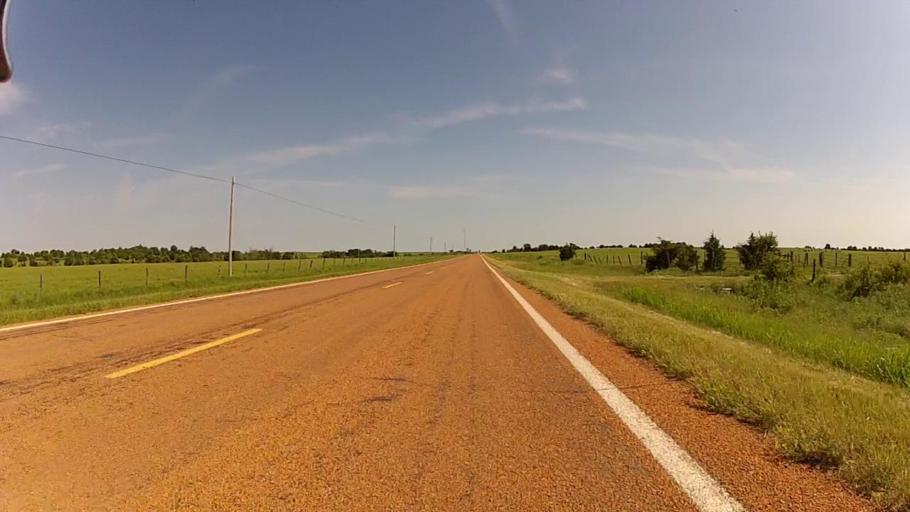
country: US
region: Kansas
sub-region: Cowley County
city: Winfield
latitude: 37.0964
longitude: -96.6437
